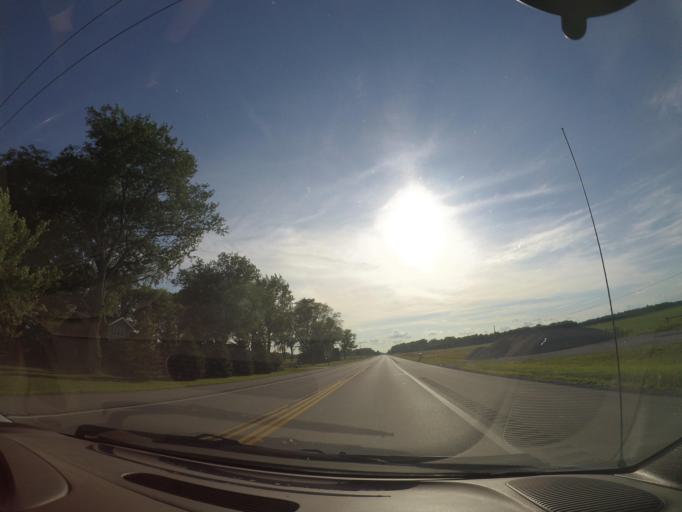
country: US
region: Ohio
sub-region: Williams County
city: Bryan
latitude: 41.4417
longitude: -84.5535
